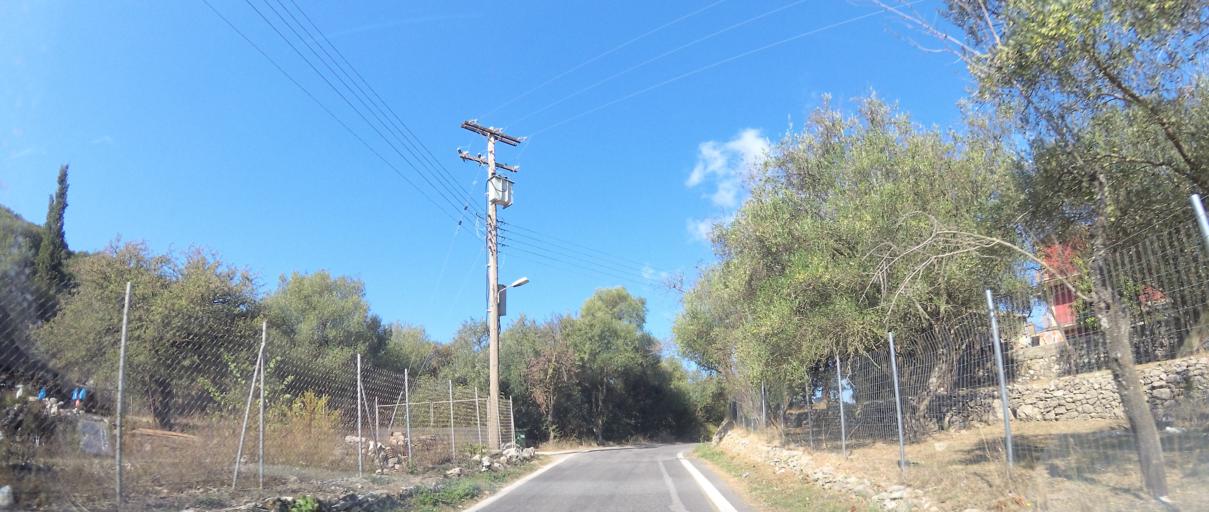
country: GR
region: Ionian Islands
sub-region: Nomos Kerkyras
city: Acharavi
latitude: 39.7219
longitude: 19.8344
